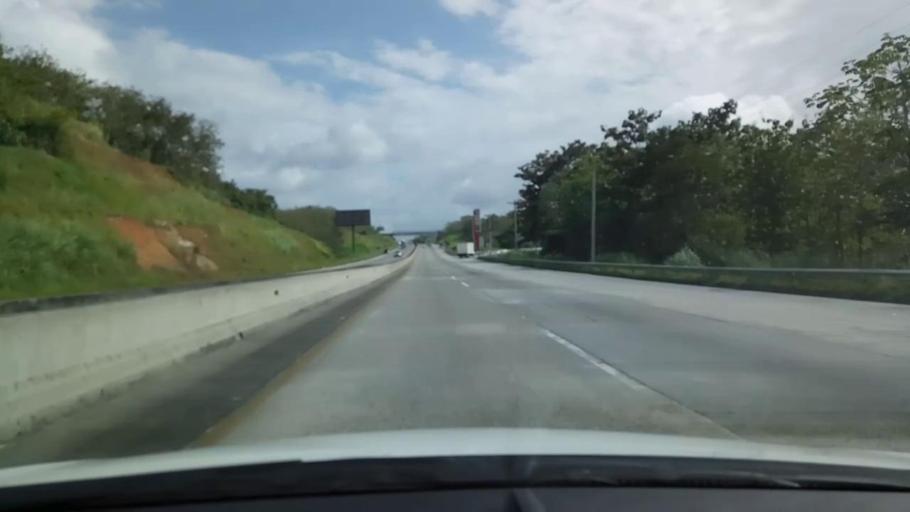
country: PA
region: Colon
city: El Giral
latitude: 9.2501
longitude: -79.6894
